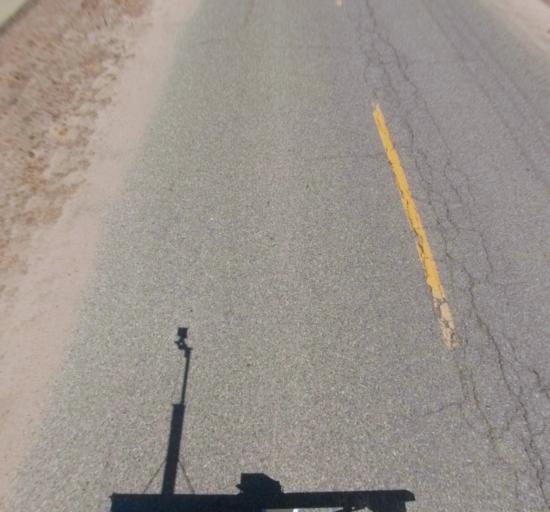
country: US
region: California
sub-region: Madera County
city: Chowchilla
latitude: 37.0338
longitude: -120.3106
